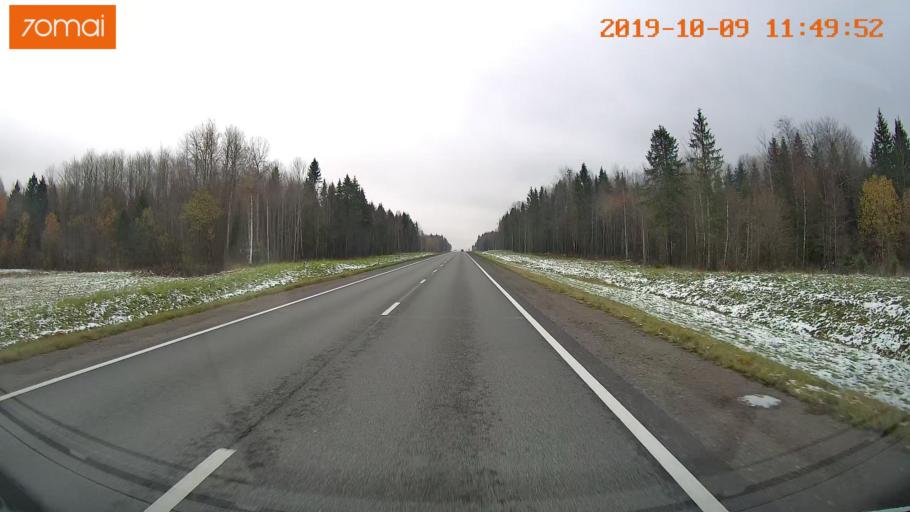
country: RU
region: Vologda
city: Gryazovets
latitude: 58.8128
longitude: 40.2372
